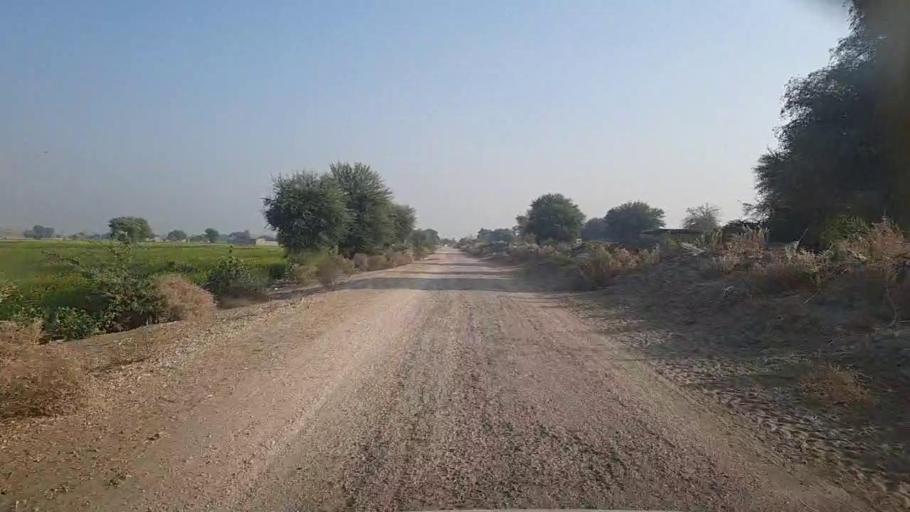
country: PK
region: Sindh
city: Karaundi
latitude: 26.7343
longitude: 68.4830
